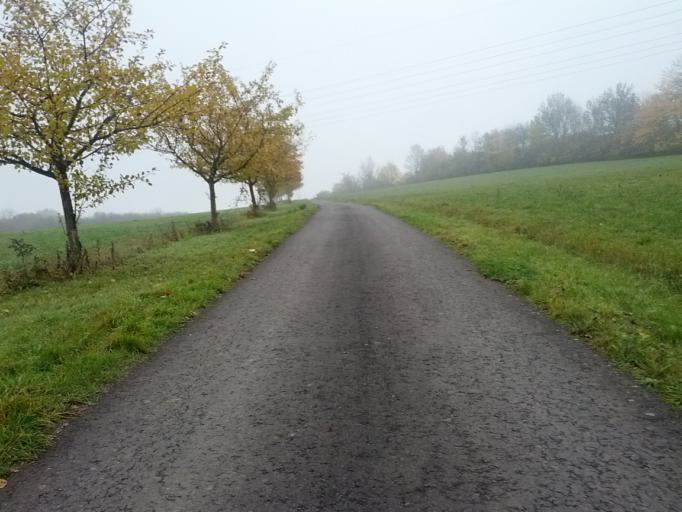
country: DE
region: Thuringia
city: Eisenach
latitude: 50.9717
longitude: 10.3721
